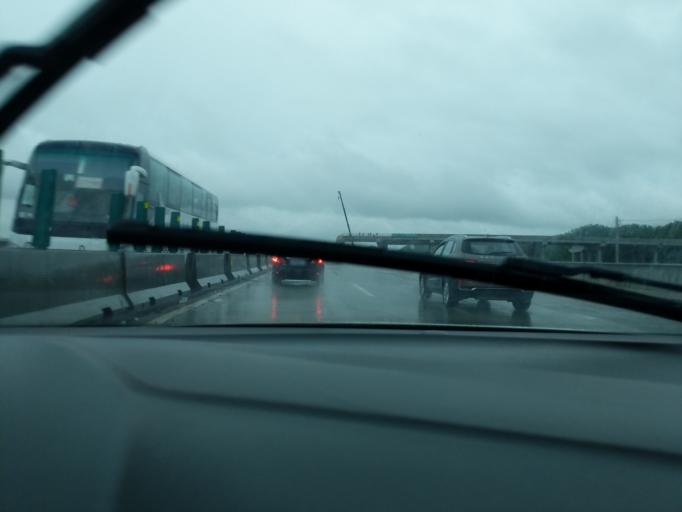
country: CN
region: Guangdong
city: Yueshan
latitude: 22.4632
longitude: 112.7135
